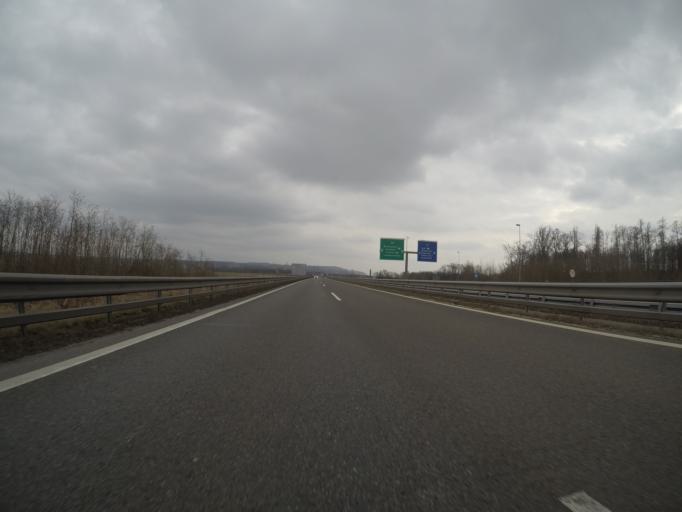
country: SI
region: Lendava-Lendva
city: Lendava
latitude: 46.5905
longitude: 16.4226
